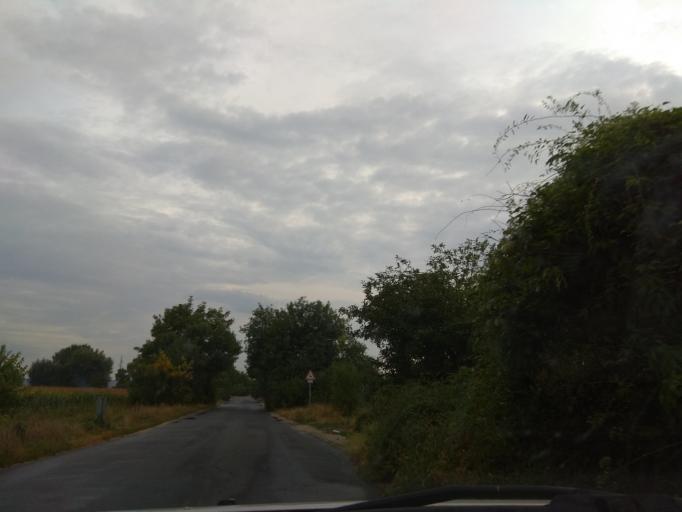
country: HU
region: Borsod-Abauj-Zemplen
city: Felsozsolca
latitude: 48.0972
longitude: 20.8330
